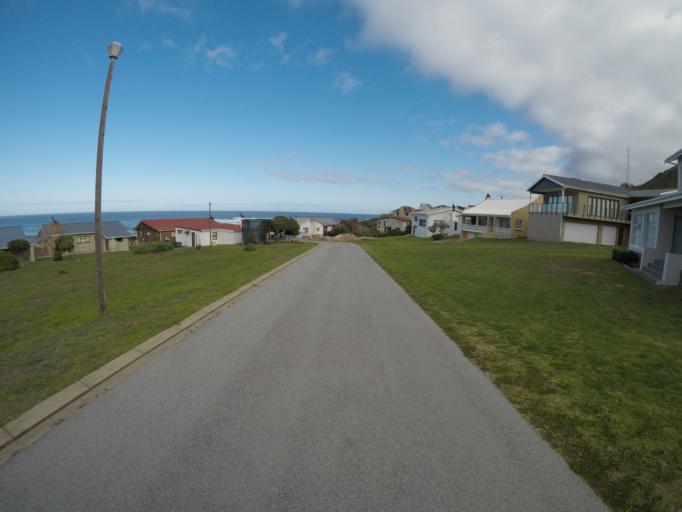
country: ZA
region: Western Cape
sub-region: Eden District Municipality
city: Riversdale
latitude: -34.4270
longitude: 21.3353
